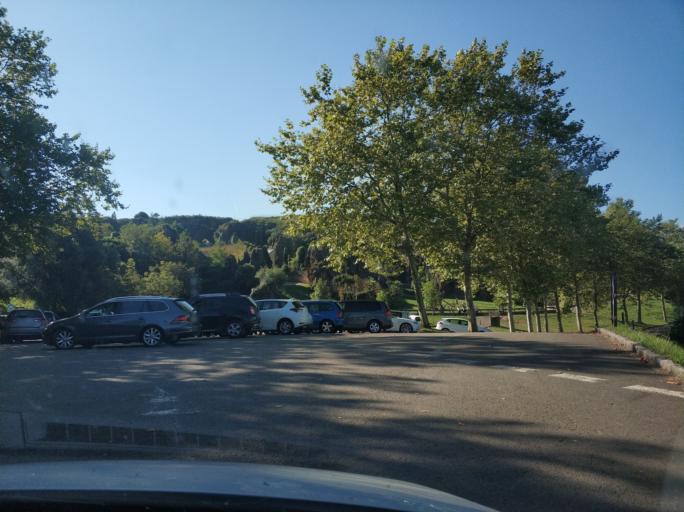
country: ES
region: Cantabria
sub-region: Provincia de Cantabria
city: Penagos
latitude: 43.3498
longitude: -3.8482
